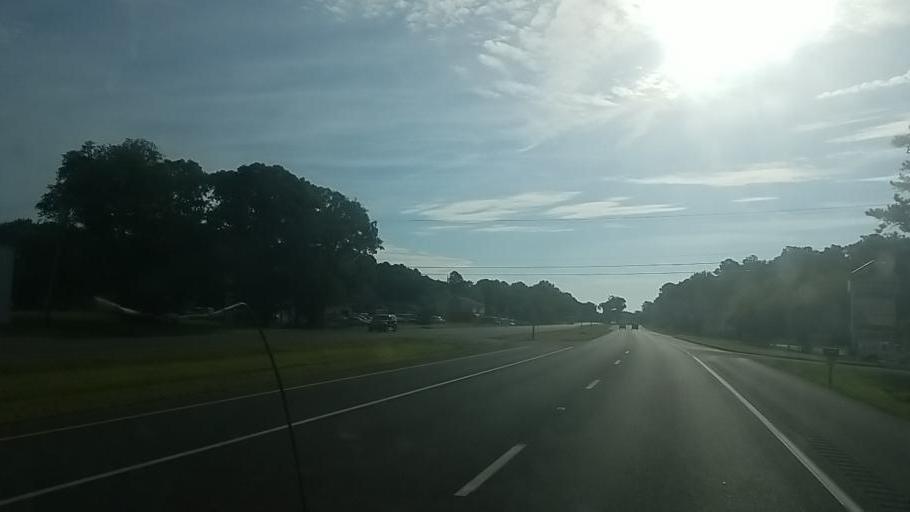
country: US
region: Maryland
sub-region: Worcester County
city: West Ocean City
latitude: 38.3372
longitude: -75.1425
